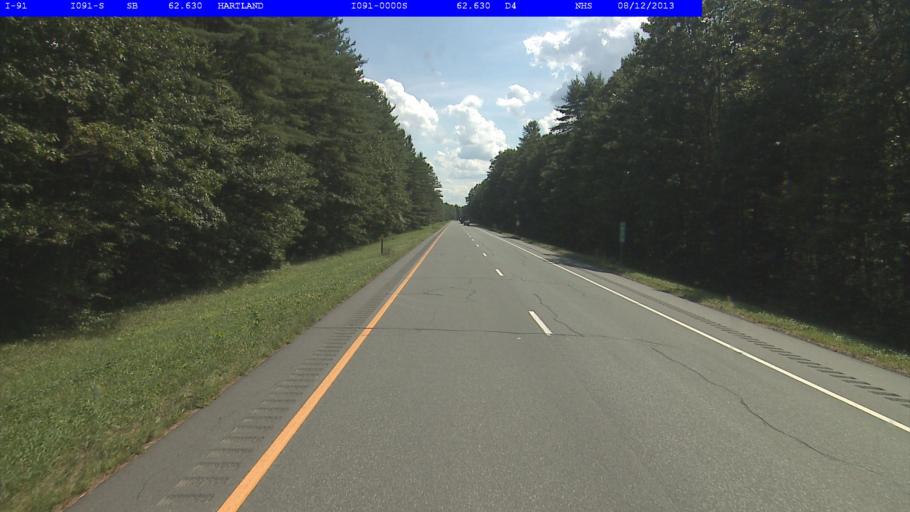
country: US
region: Vermont
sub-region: Windsor County
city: Windsor
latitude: 43.5554
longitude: -72.3855
